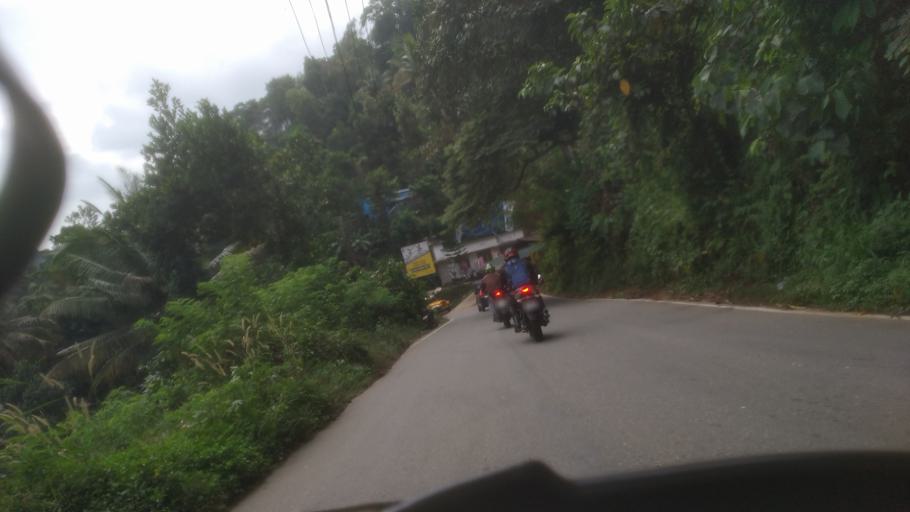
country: IN
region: Kerala
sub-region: Idukki
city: Munnar
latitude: 9.9825
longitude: 76.9992
